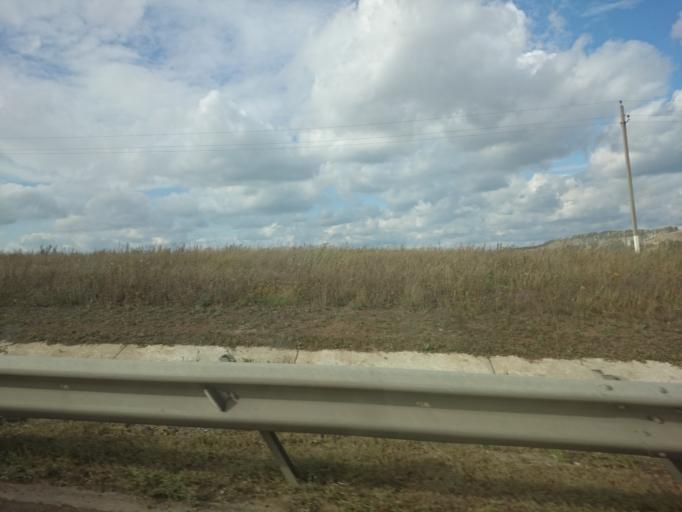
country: RU
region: Samara
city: Kamyshla
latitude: 54.0716
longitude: 52.1993
